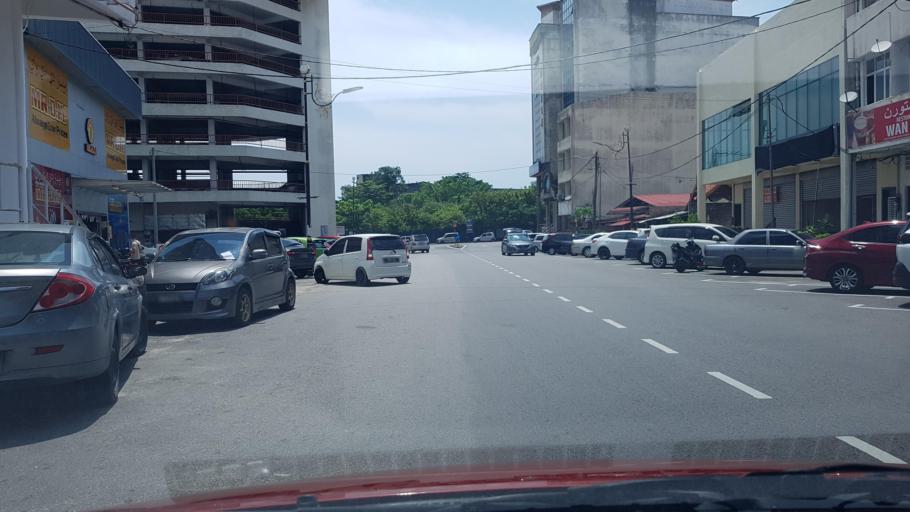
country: MY
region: Terengganu
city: Kuala Terengganu
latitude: 5.3315
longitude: 103.1345
